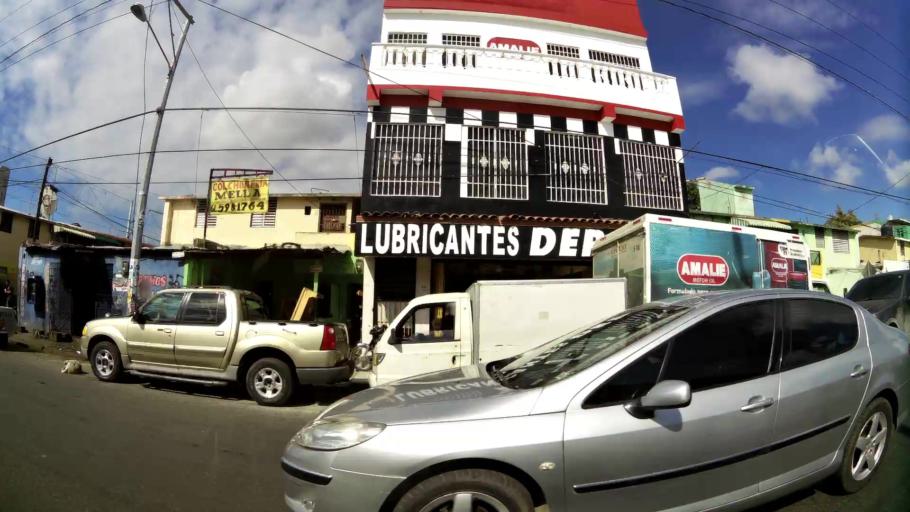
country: DO
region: Santo Domingo
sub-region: Santo Domingo
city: Santo Domingo Este
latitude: 18.4998
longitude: -69.8604
